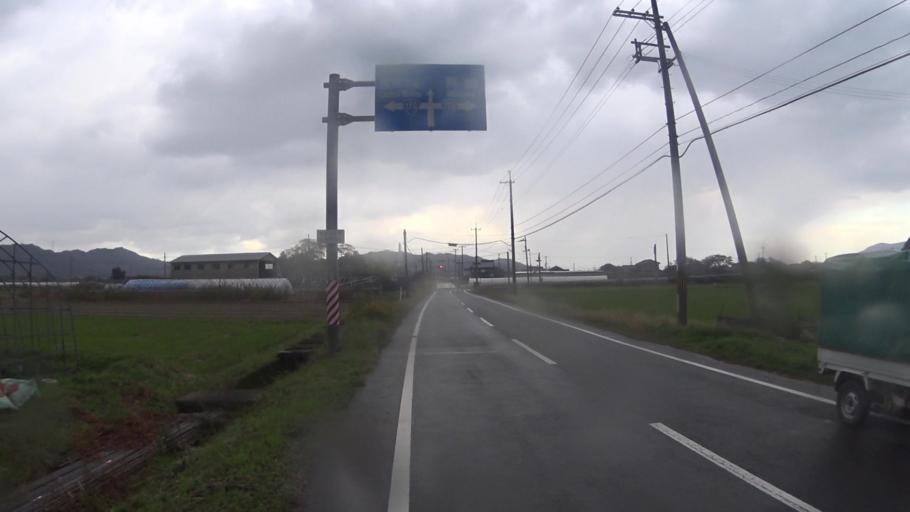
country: JP
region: Kyoto
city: Miyazu
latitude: 35.5354
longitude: 135.2392
